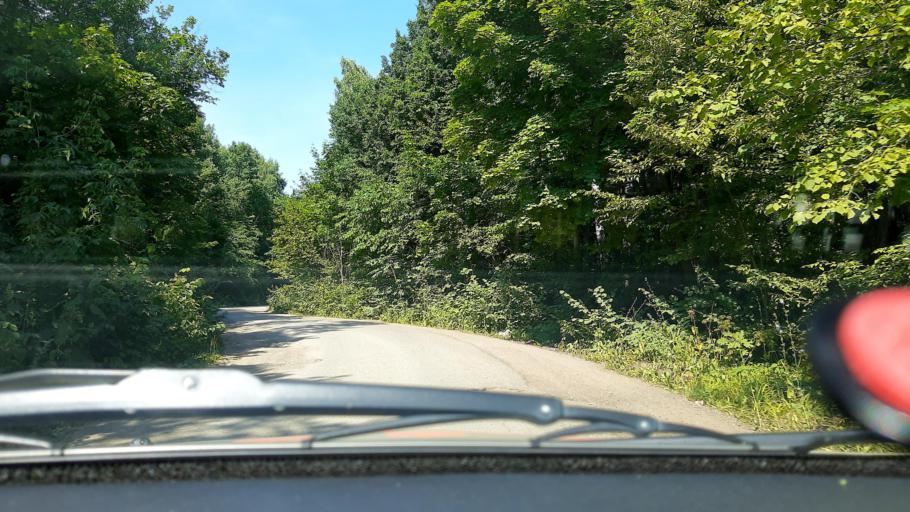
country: RU
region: Bashkortostan
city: Karmaskaly
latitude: 54.3822
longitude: 55.9150
